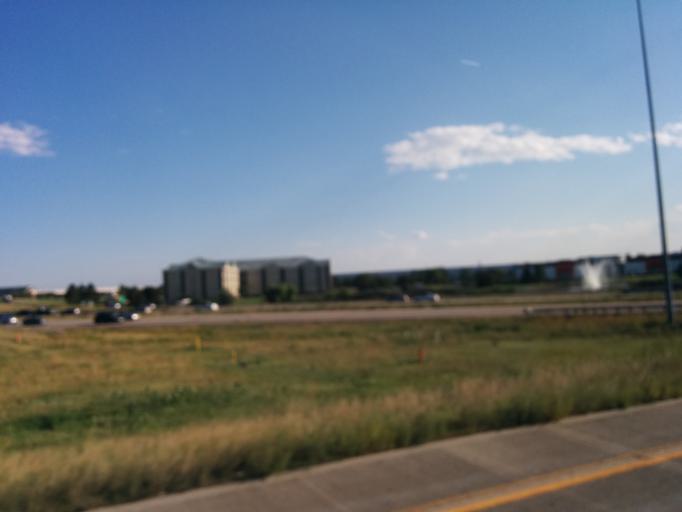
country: US
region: Colorado
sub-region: Adams County
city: Aurora
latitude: 39.7676
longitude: -104.7935
